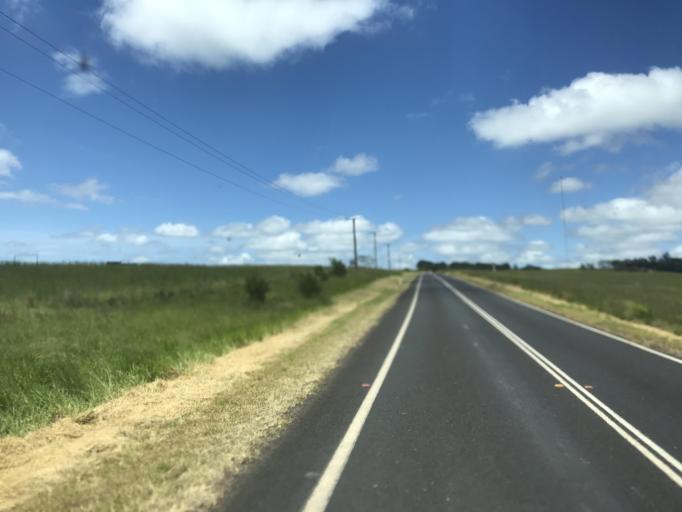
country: AU
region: Queensland
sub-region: Tablelands
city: Ravenshoe
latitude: -17.4894
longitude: 145.4737
